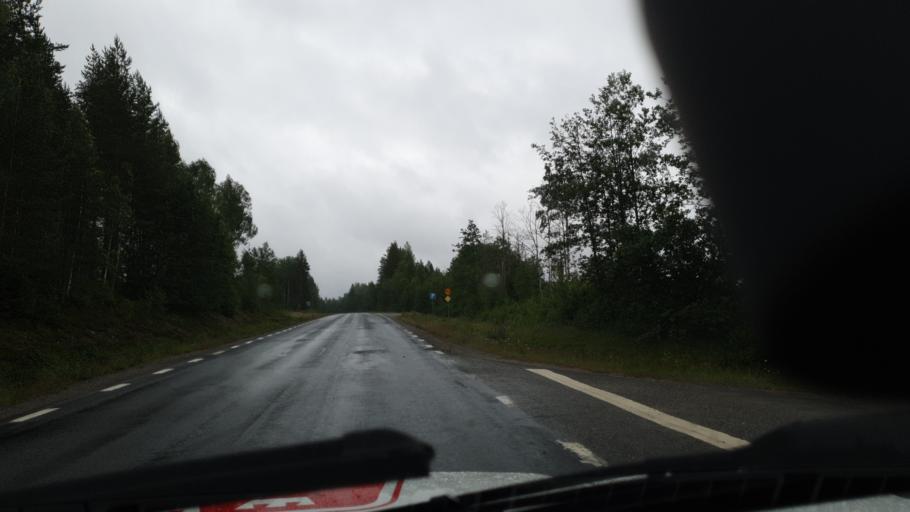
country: SE
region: Vaesterbotten
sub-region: Vannas Kommun
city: Vaennaes
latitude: 63.7715
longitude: 19.7023
